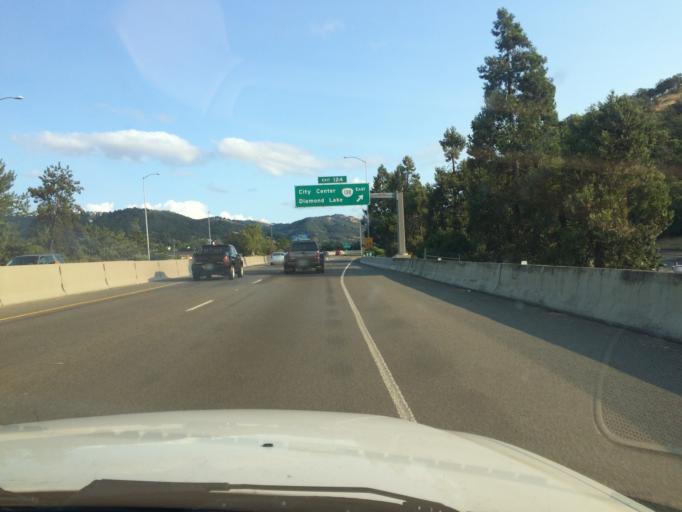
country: US
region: Oregon
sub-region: Douglas County
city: Roseburg
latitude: 43.2152
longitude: -123.3561
